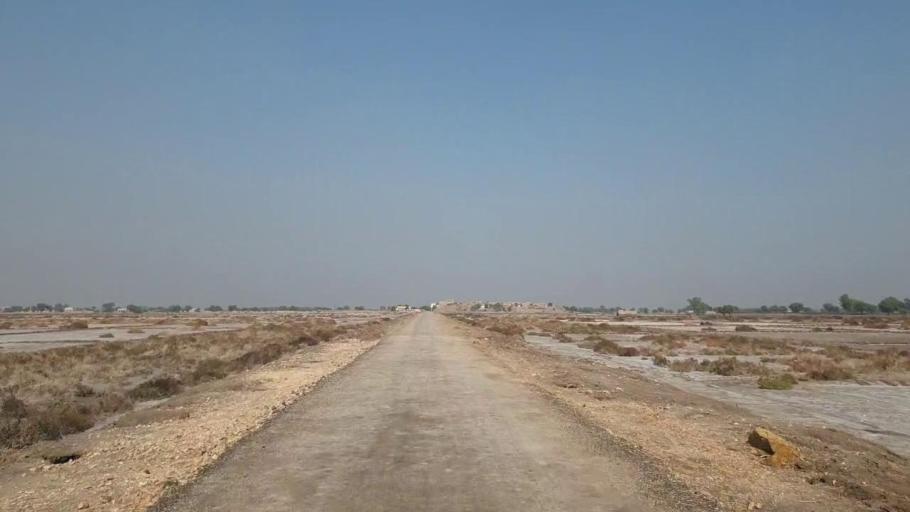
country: PK
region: Sindh
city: Sehwan
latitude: 26.4212
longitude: 67.7958
